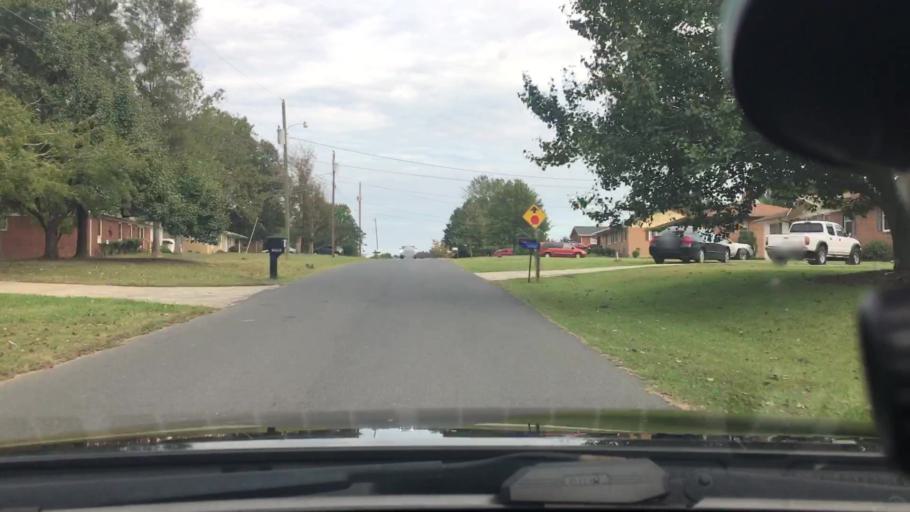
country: US
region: North Carolina
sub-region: Stanly County
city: Albemarle
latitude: 35.3410
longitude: -80.1528
